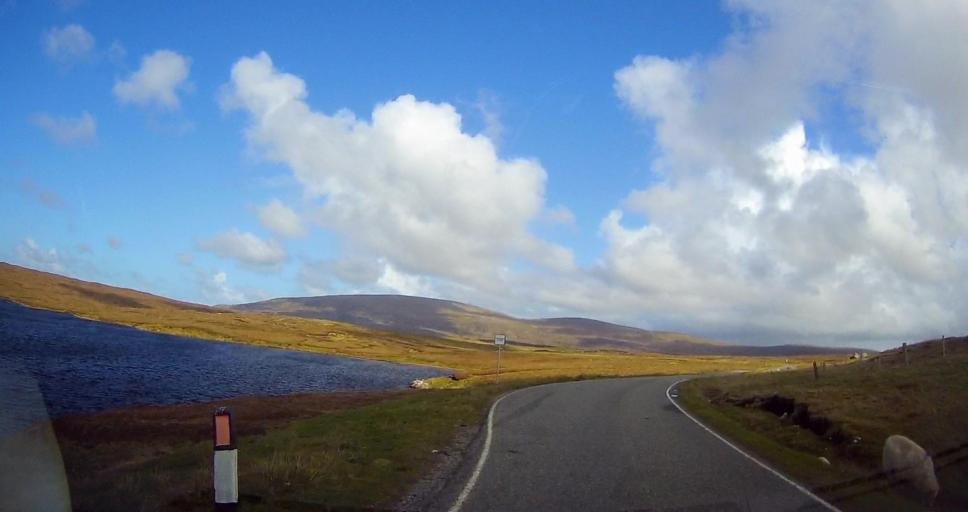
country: GB
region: Scotland
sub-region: Shetland Islands
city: Lerwick
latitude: 60.4925
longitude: -1.3913
